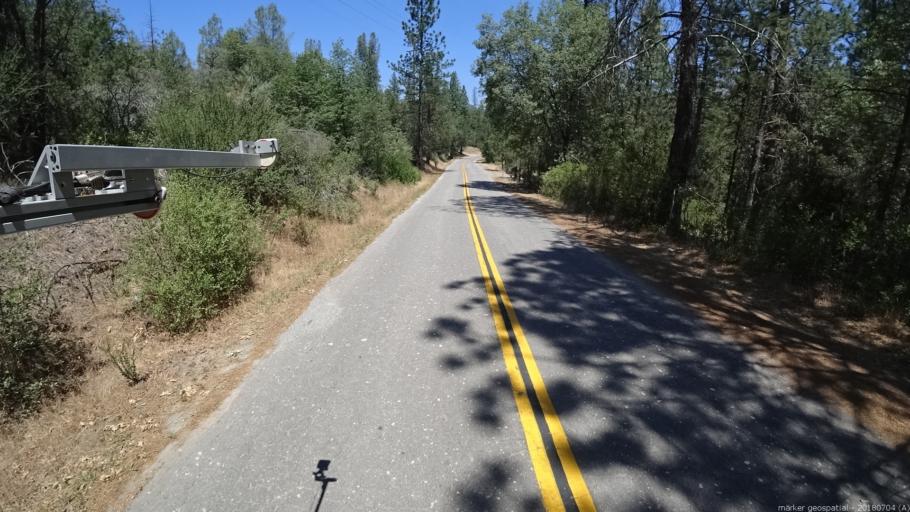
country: US
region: California
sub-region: Fresno County
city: Auberry
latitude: 37.2322
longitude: -119.4994
